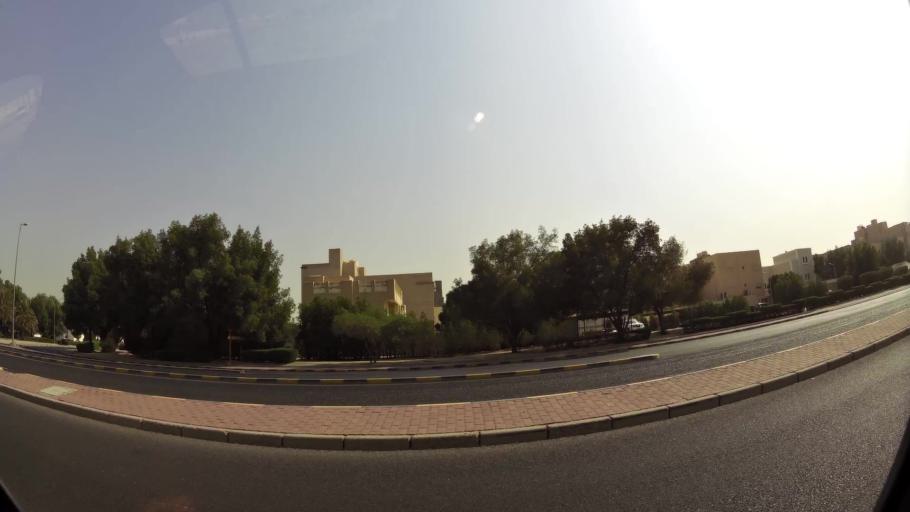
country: KW
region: Al Asimah
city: Ar Rabiyah
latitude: 29.2877
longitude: 47.9281
